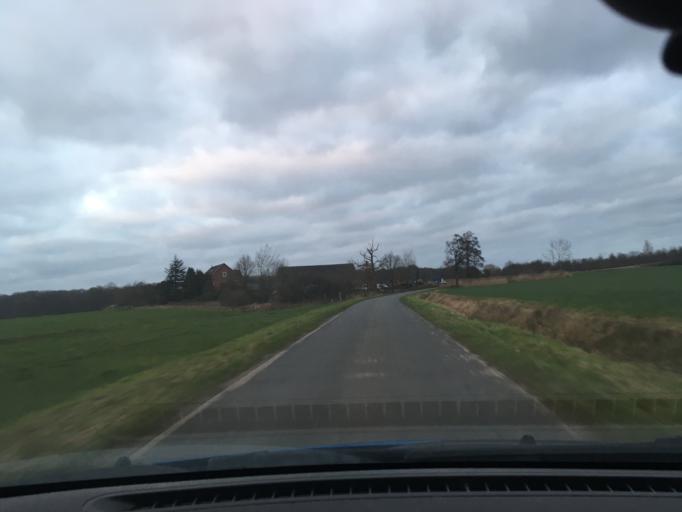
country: DE
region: Schleswig-Holstein
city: Kaaks
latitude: 54.0019
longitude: 9.4723
